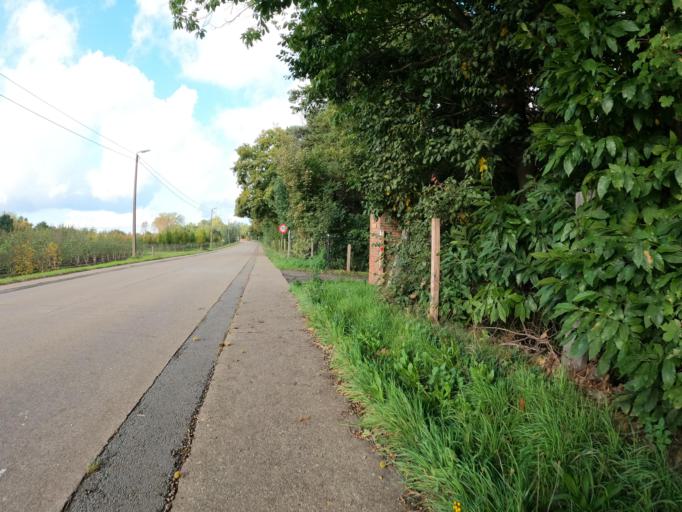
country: BE
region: Flanders
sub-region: Provincie Vlaams-Brabant
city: Begijnendijk
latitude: 50.9772
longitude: 4.7816
